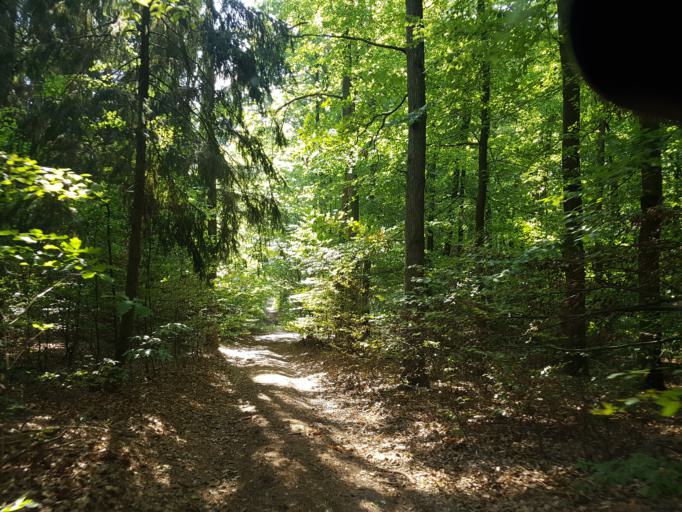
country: DE
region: Brandenburg
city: Gorzke
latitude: 52.0732
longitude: 12.3648
